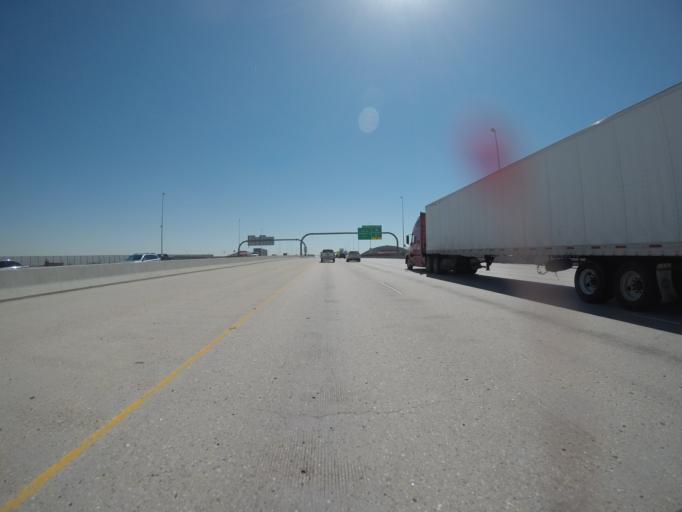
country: US
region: Colorado
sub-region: Denver County
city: Denver
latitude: 39.7796
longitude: -104.9755
